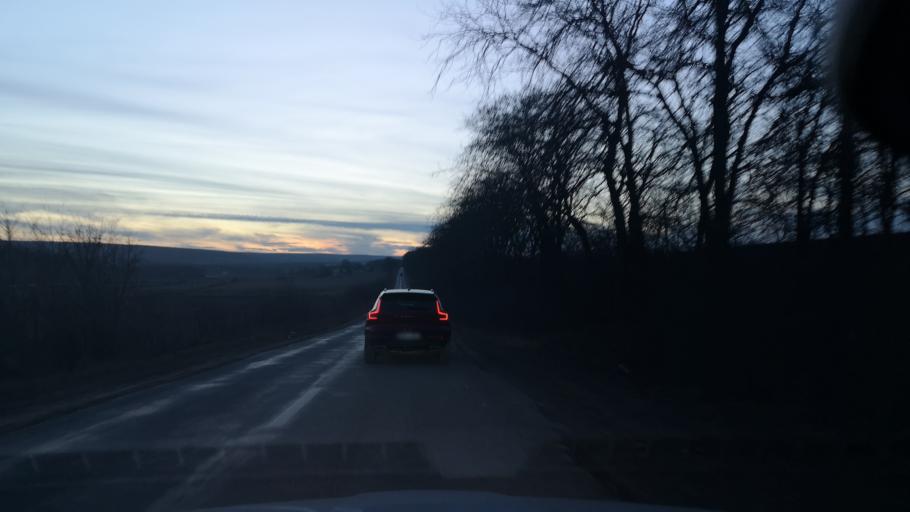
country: MD
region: Orhei
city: Orhei
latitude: 47.2982
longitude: 28.9088
